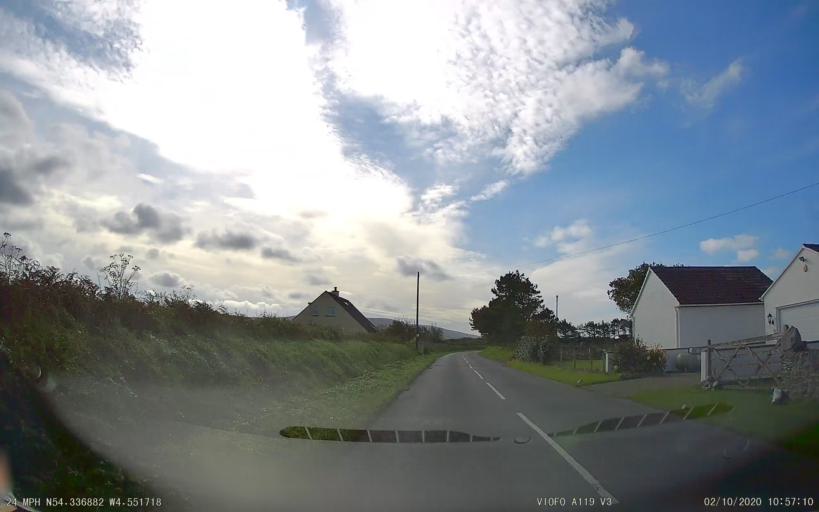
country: IM
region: Ramsey
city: Ramsey
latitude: 54.3367
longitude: -4.5513
